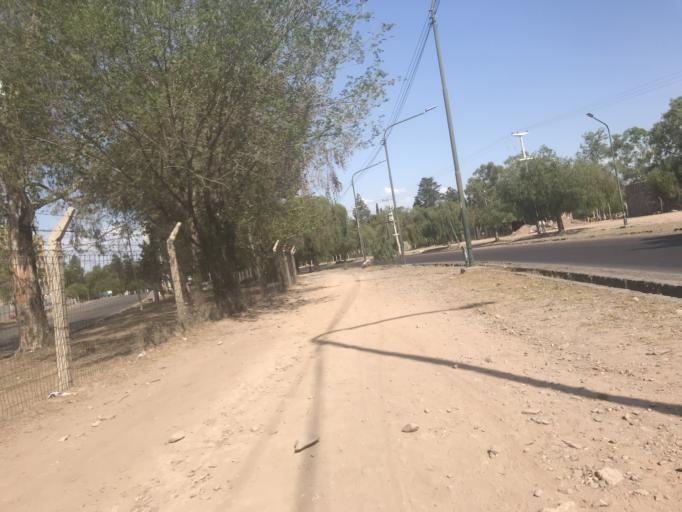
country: AR
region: Mendoza
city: Mendoza
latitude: -32.8828
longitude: -68.8803
